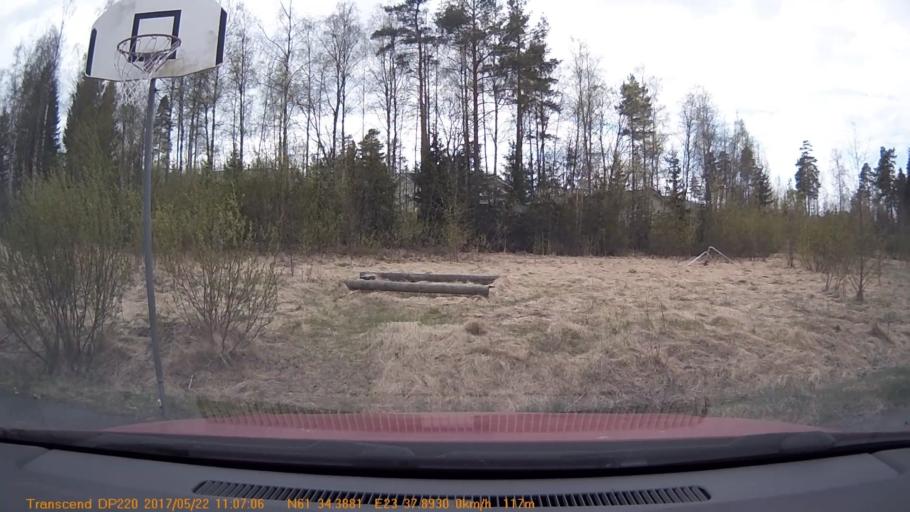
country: FI
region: Pirkanmaa
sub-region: Tampere
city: Yloejaervi
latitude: 61.5731
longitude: 23.6316
